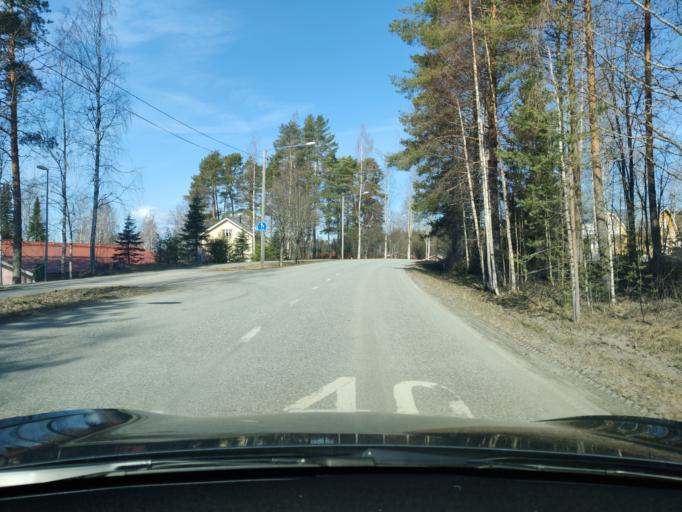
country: FI
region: Northern Savo
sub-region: Kuopio
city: Vehmersalmi
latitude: 62.7629
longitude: 28.0232
